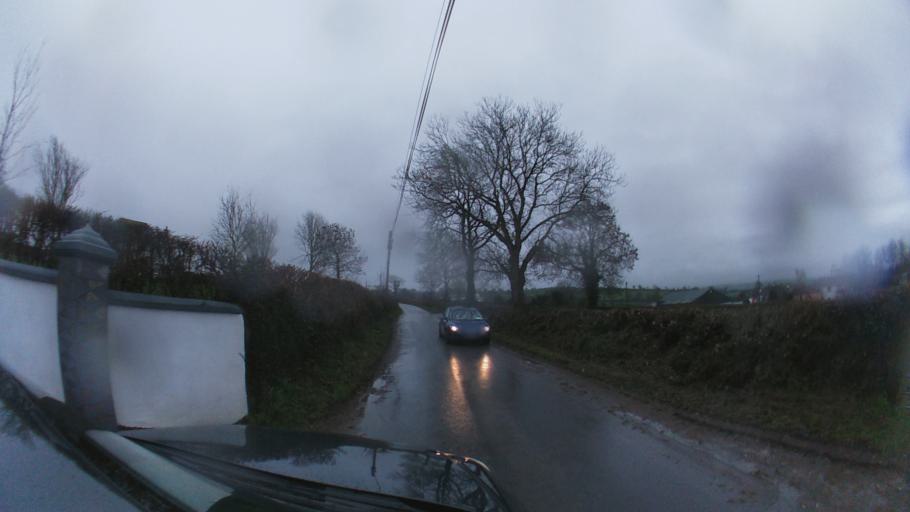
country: IE
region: Leinster
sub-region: Kilkenny
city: Graiguenamanagh
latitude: 52.5967
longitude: -6.9934
